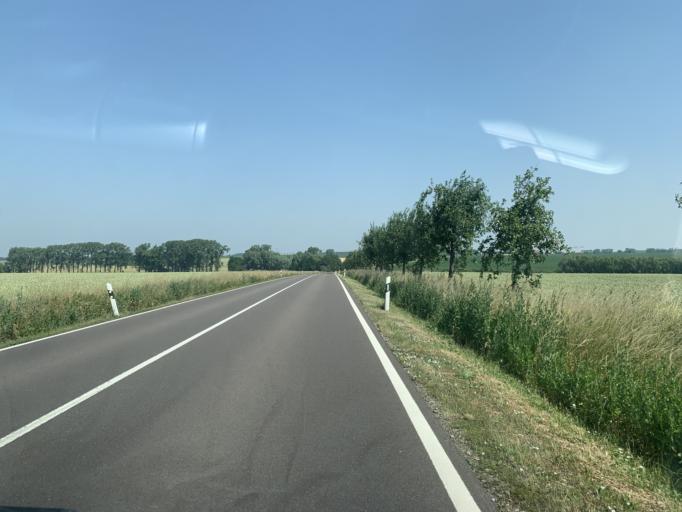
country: DE
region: Saxony-Anhalt
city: Altenhausen
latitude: 52.2446
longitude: 11.2454
